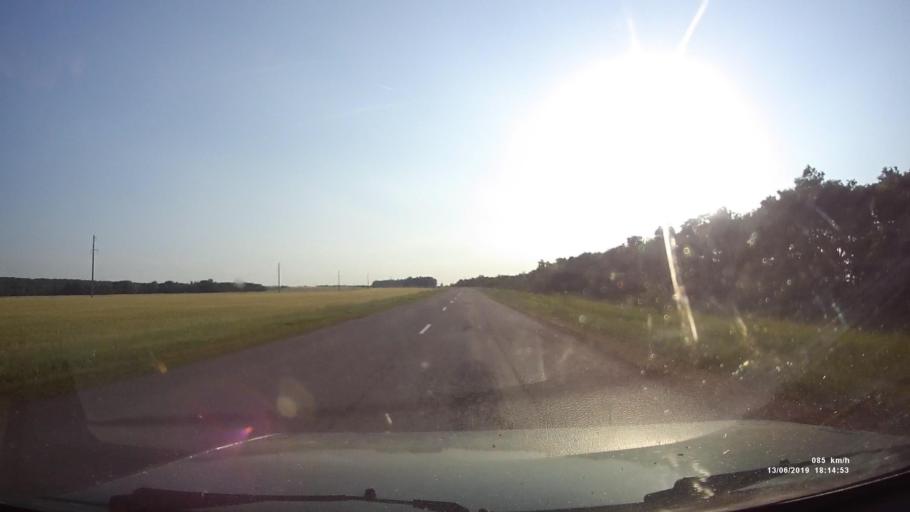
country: RU
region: Rostov
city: Kazanskaya
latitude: 49.9327
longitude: 41.3672
